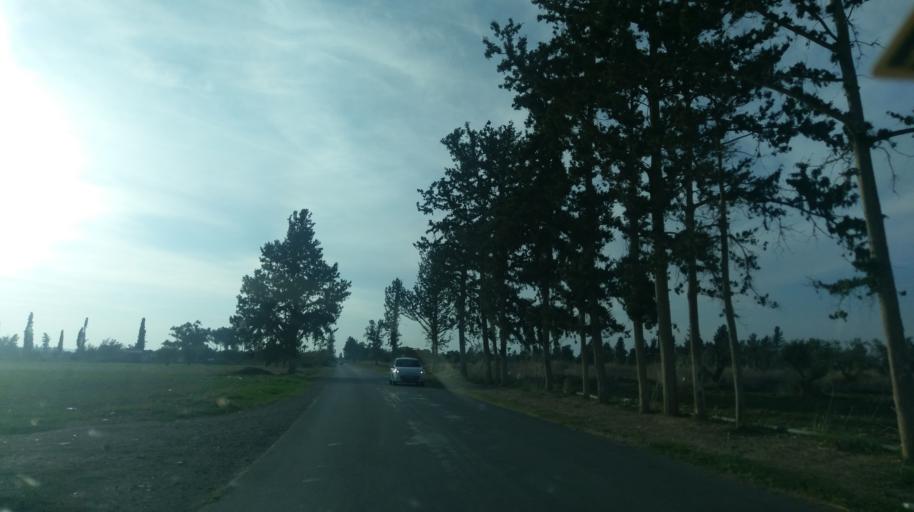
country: CY
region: Larnaka
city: Pergamos
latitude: 35.1057
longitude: 33.7001
